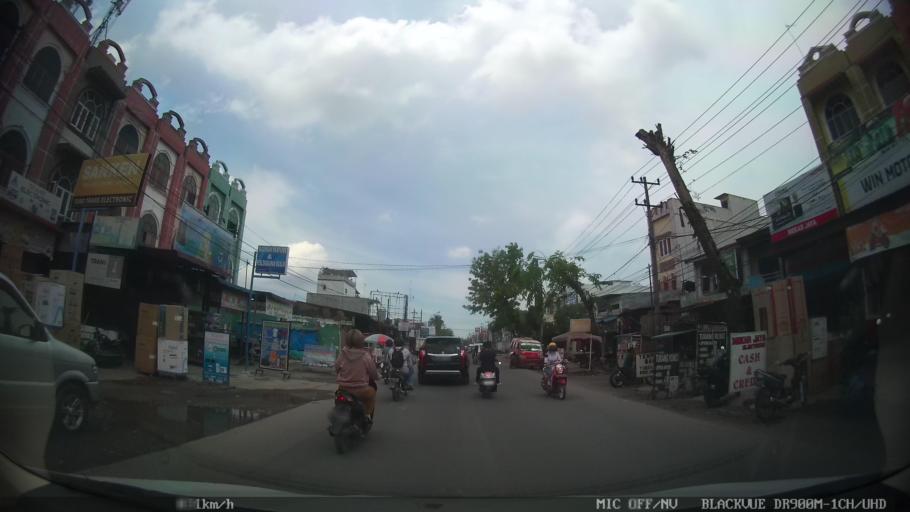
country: ID
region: North Sumatra
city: Labuhan Deli
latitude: 3.6958
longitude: 98.6563
